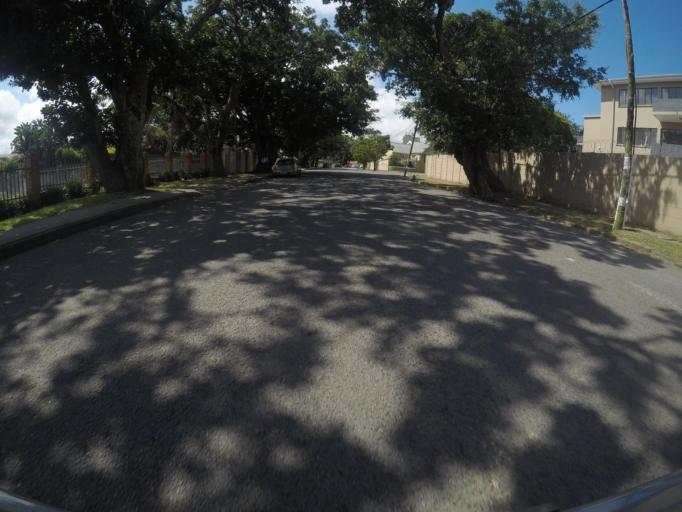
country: ZA
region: Eastern Cape
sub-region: Buffalo City Metropolitan Municipality
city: East London
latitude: -33.0020
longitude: 27.8957
